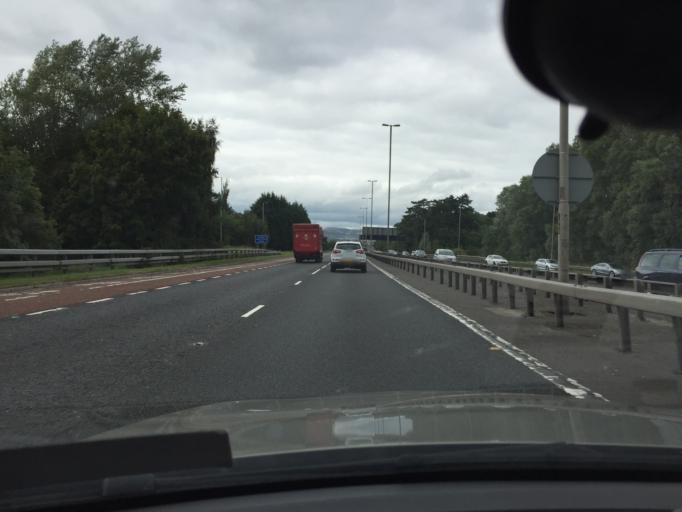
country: GB
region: Northern Ireland
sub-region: Lisburn District
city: Lisburn
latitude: 54.5585
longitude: -5.9951
